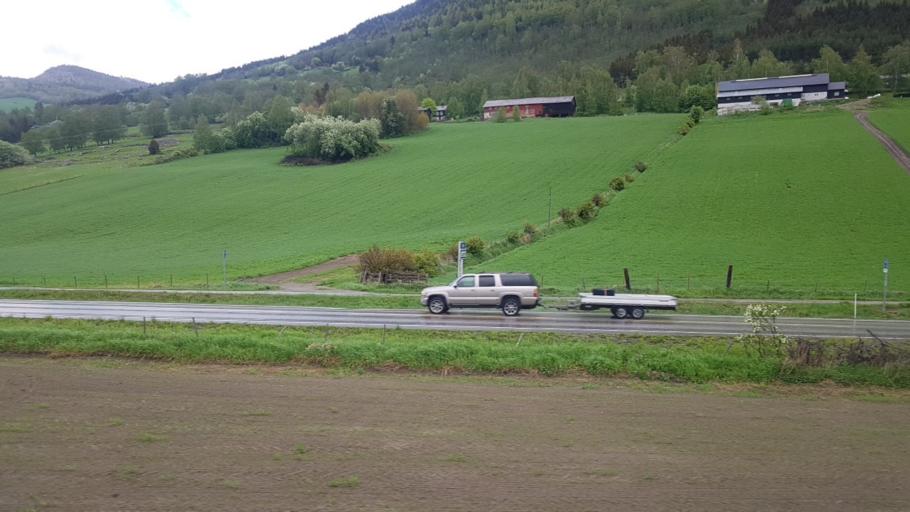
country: NO
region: Oppland
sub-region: Nord-Fron
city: Vinstra
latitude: 61.6638
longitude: 9.6796
